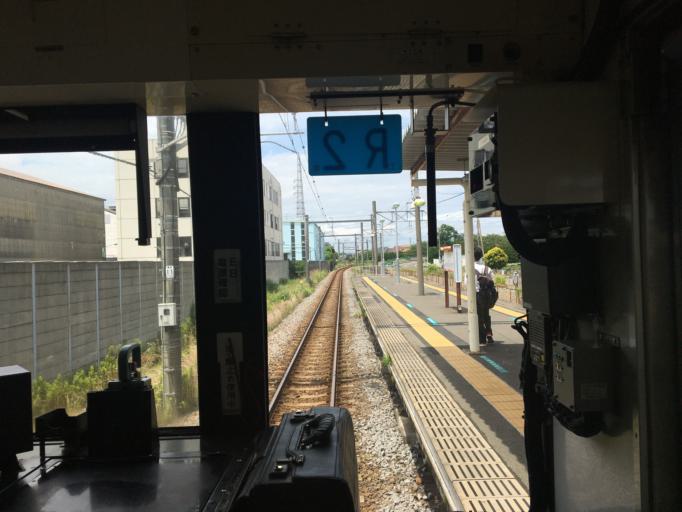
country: JP
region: Kanagawa
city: Chigasaki
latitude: 35.3397
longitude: 139.4073
